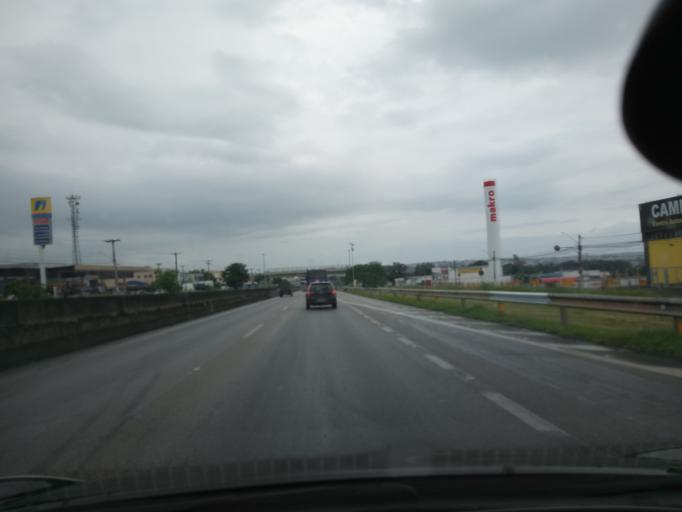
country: BR
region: Sao Paulo
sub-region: Campinas
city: Campinas
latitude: -22.9490
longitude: -47.0909
